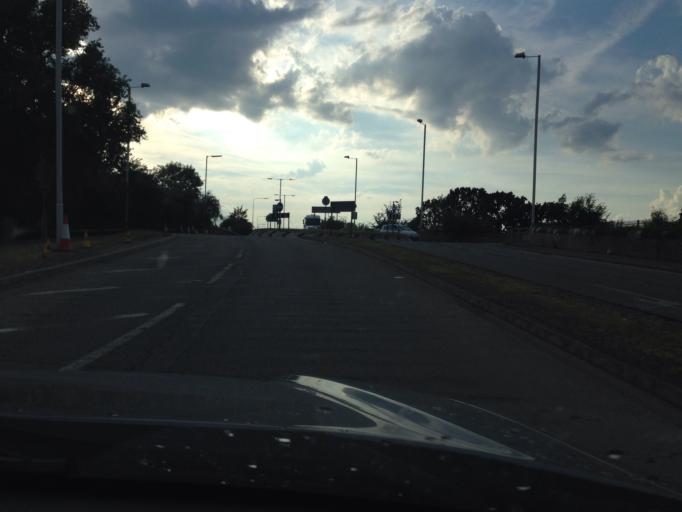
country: GB
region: England
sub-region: Greater London
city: Uxbridge
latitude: 51.5525
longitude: -0.4502
